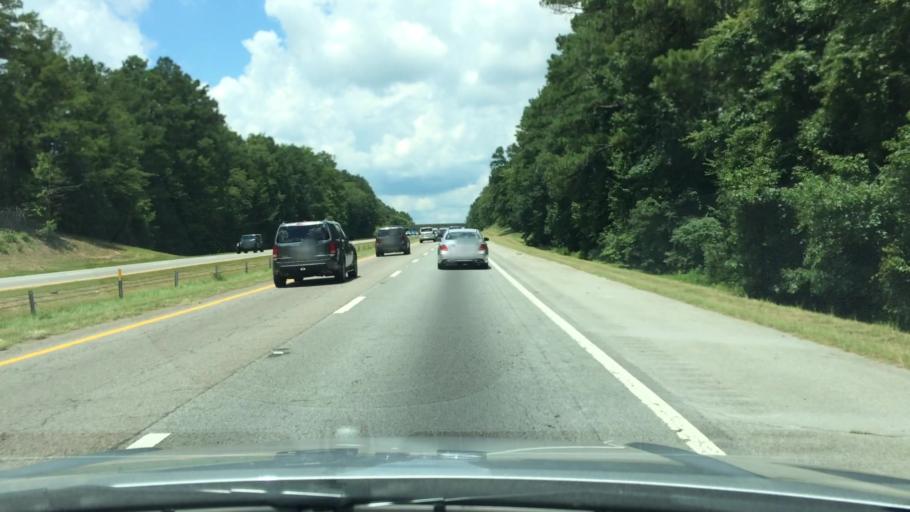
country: US
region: South Carolina
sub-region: Newberry County
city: Prosperity
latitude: 34.2496
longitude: -81.4824
